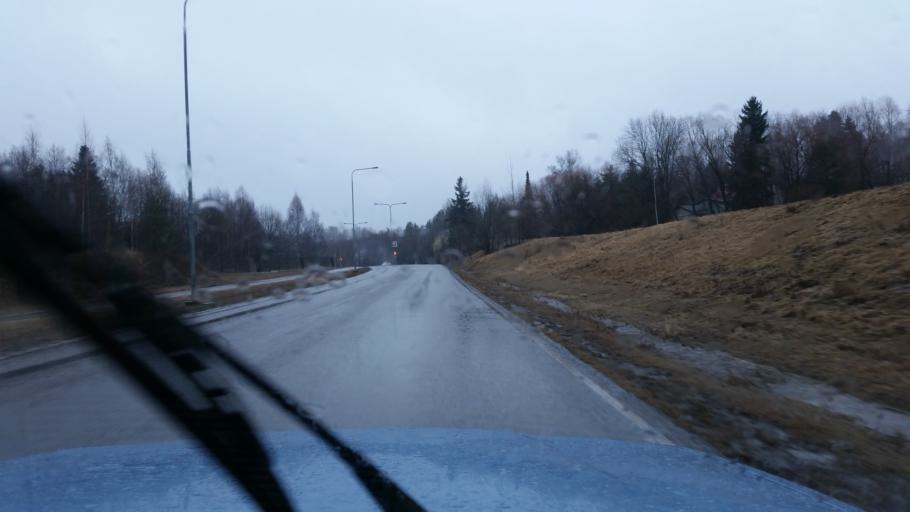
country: FI
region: Pirkanmaa
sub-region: Tampere
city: Tampere
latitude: 61.4738
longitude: 23.7941
